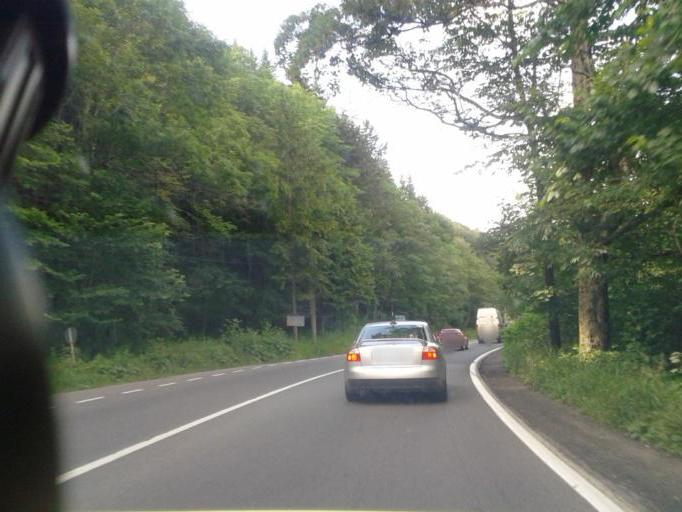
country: RO
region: Prahova
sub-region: Oras Busteni
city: Poiana Tapului
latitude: 45.3842
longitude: 25.5374
